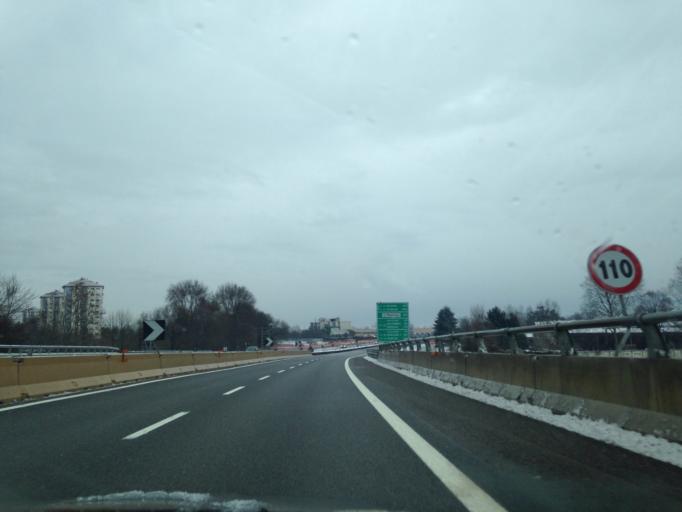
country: IT
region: Piedmont
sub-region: Provincia di Torino
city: Settimo Torinese
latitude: 45.1238
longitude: 7.7145
